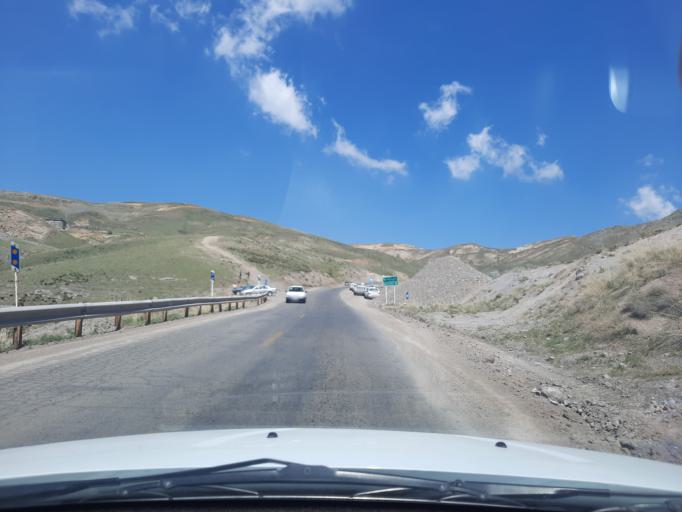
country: IR
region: Qazvin
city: Qazvin
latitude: 36.3738
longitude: 50.2060
